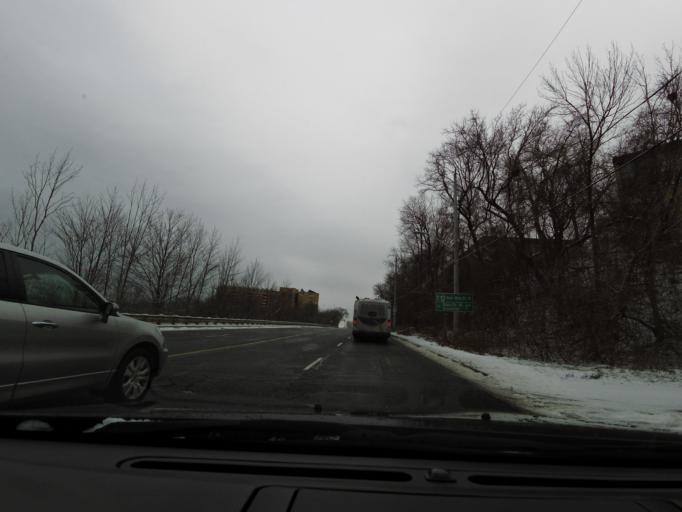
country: CA
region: Ontario
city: Ancaster
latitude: 43.2578
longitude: -79.9384
